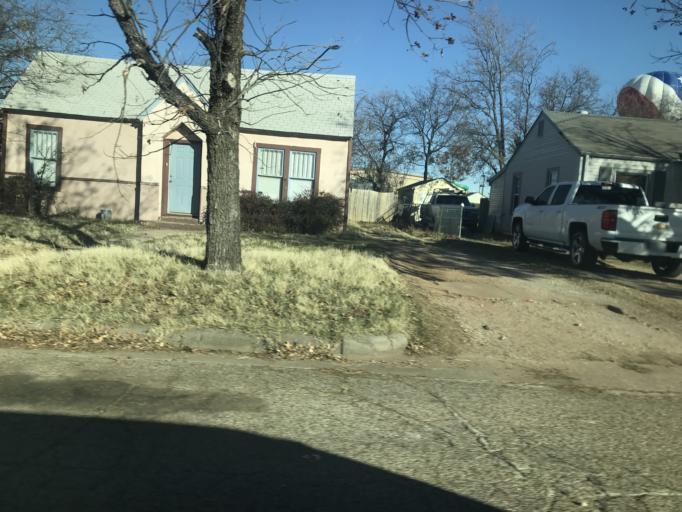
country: US
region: Texas
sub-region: Taylor County
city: Abilene
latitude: 32.4386
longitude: -99.7568
